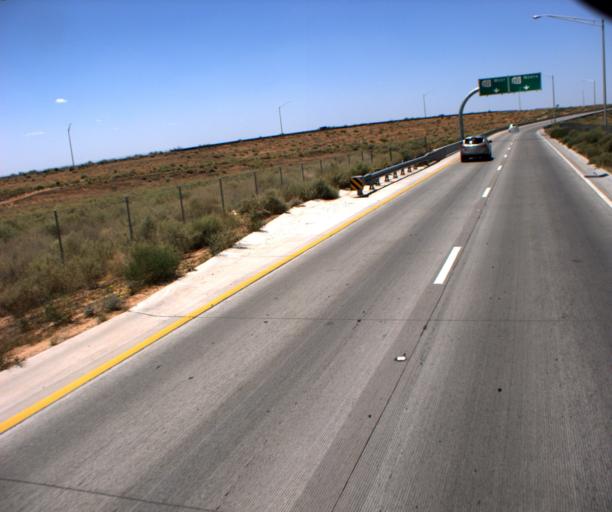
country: US
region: Arizona
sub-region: Maricopa County
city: Queen Creek
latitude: 33.3185
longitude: -111.6367
